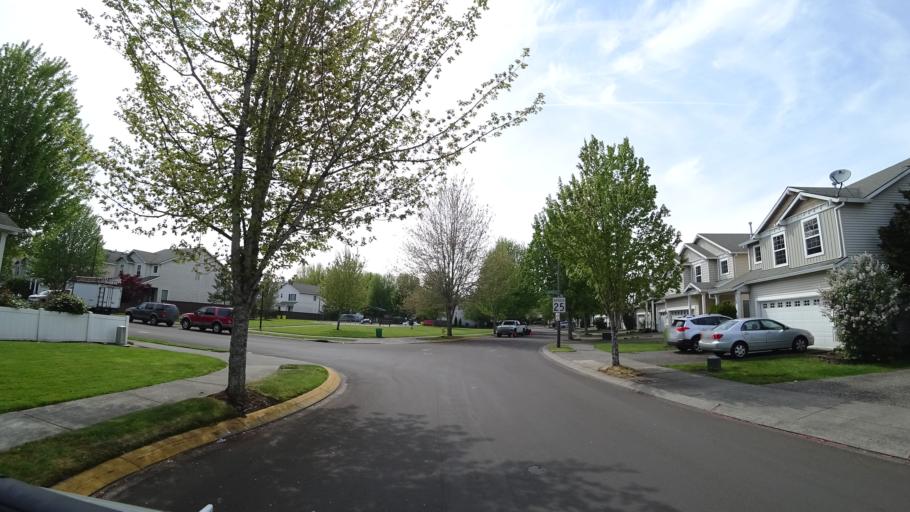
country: US
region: Oregon
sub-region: Washington County
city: Rockcreek
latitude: 45.5216
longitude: -122.9291
